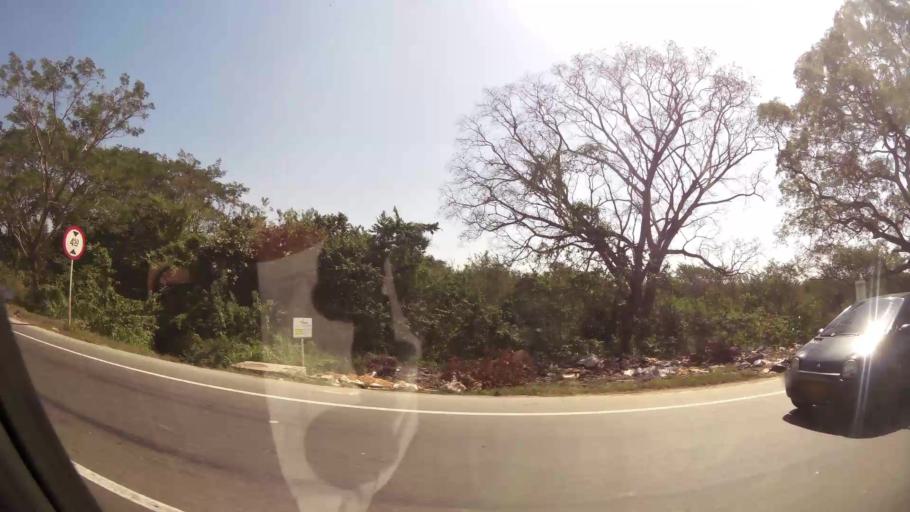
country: CO
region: Bolivar
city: Turbaco
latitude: 10.3808
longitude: -75.4507
